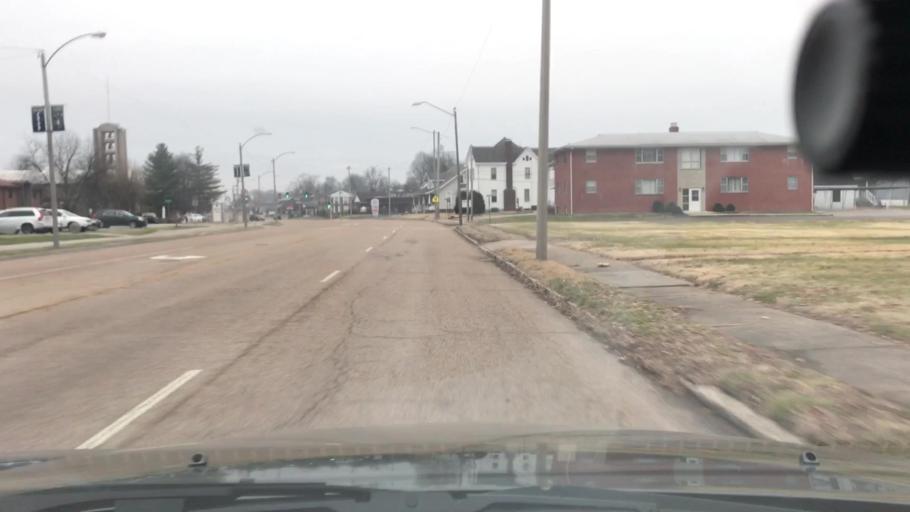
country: US
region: Illinois
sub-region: Saint Clair County
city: Swansea
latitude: 38.5475
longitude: -90.0334
